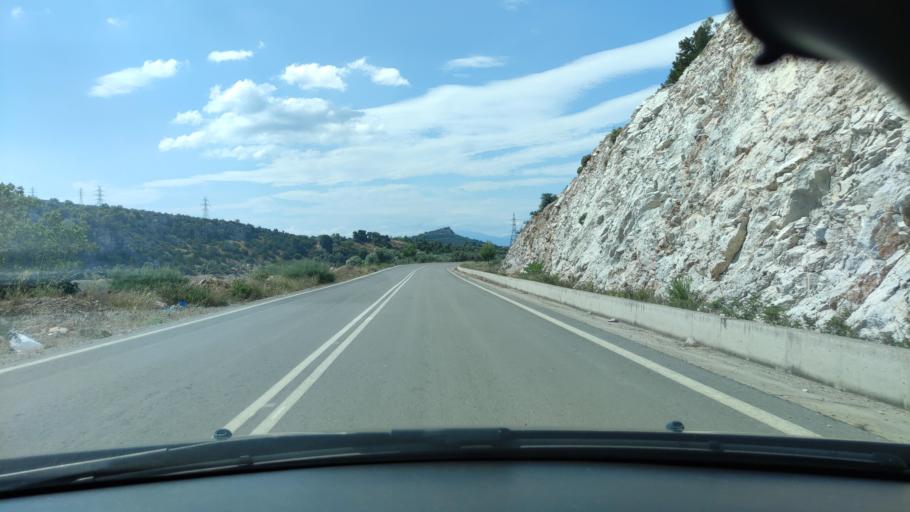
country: GR
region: Central Greece
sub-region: Nomos Evvoias
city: Afration
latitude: 38.4686
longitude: 23.6850
